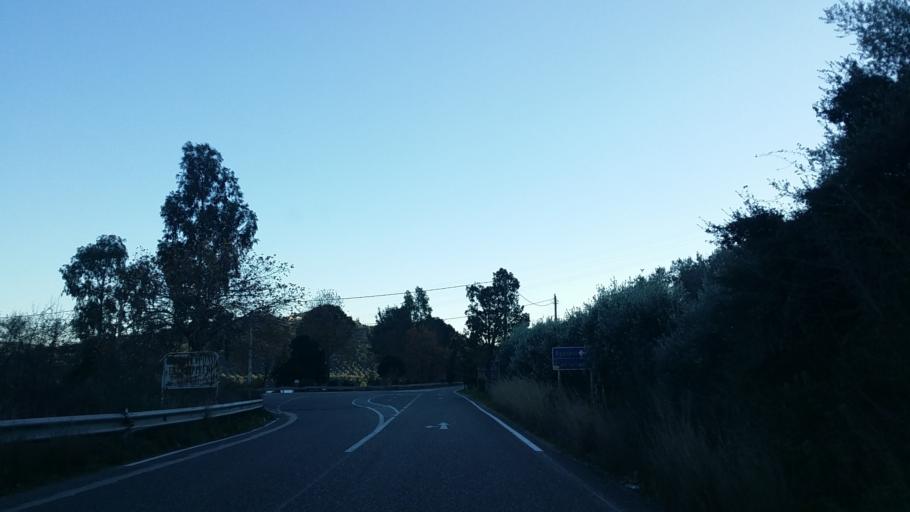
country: GR
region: West Greece
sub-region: Nomos Aitolias kai Akarnanias
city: Lepenou
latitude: 38.7135
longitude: 21.3362
